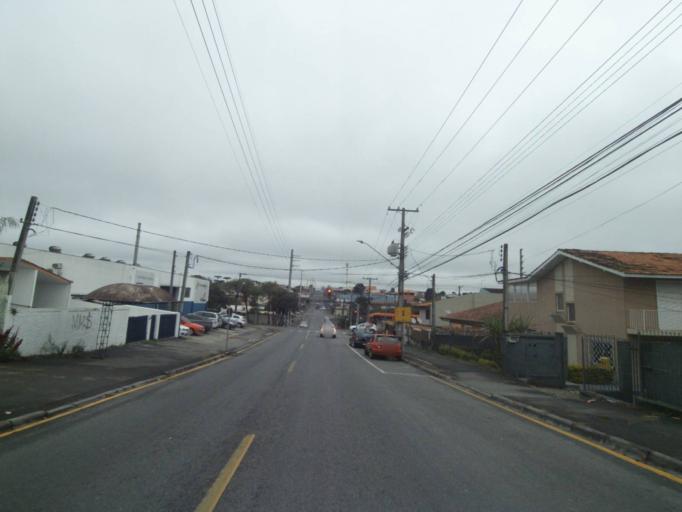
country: BR
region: Parana
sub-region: Curitiba
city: Curitiba
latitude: -25.5131
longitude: -49.3045
